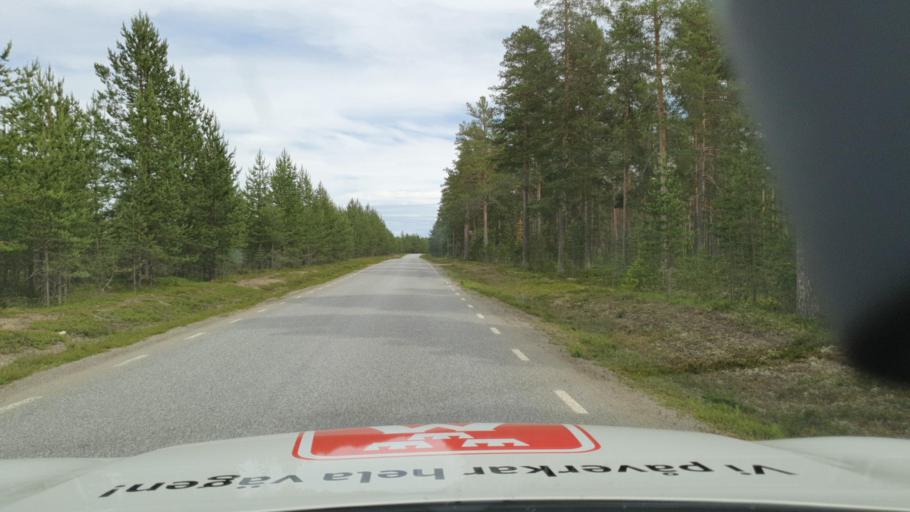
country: SE
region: Vaesterbotten
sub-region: Skelleftea Kommun
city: Burtraesk
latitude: 64.5053
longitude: 20.7860
